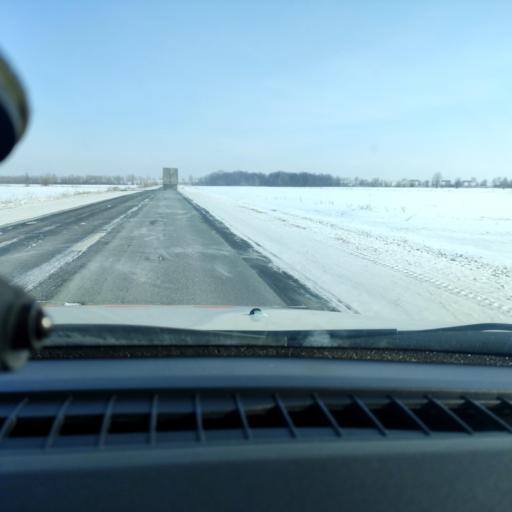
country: RU
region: Samara
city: Smyshlyayevka
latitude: 53.1857
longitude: 50.4996
